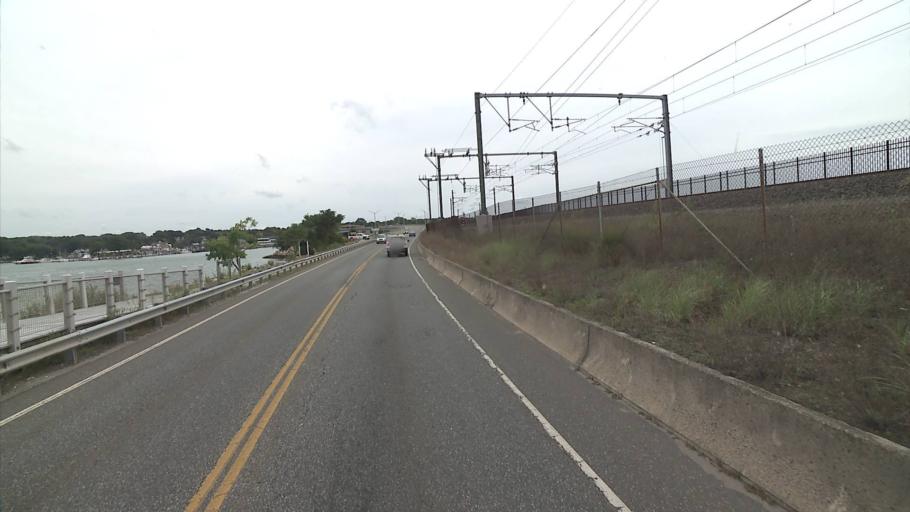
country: US
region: Connecticut
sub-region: New London County
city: Niantic
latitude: 41.3245
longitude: -72.1822
